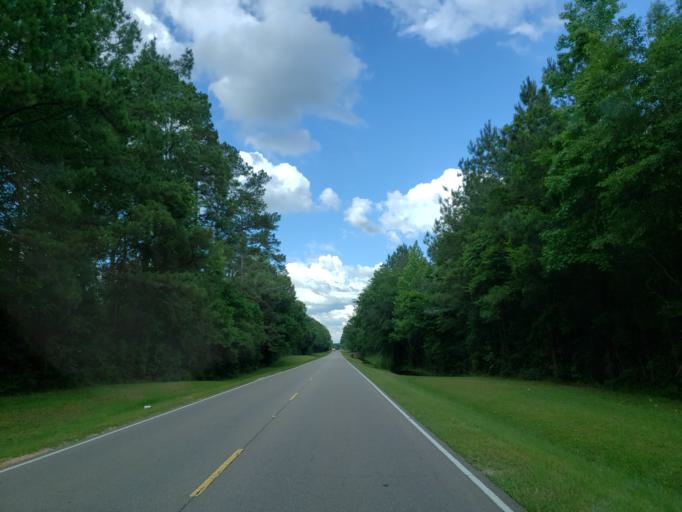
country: US
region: Mississippi
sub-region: Forrest County
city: Hattiesburg
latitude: 31.2592
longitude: -89.2324
